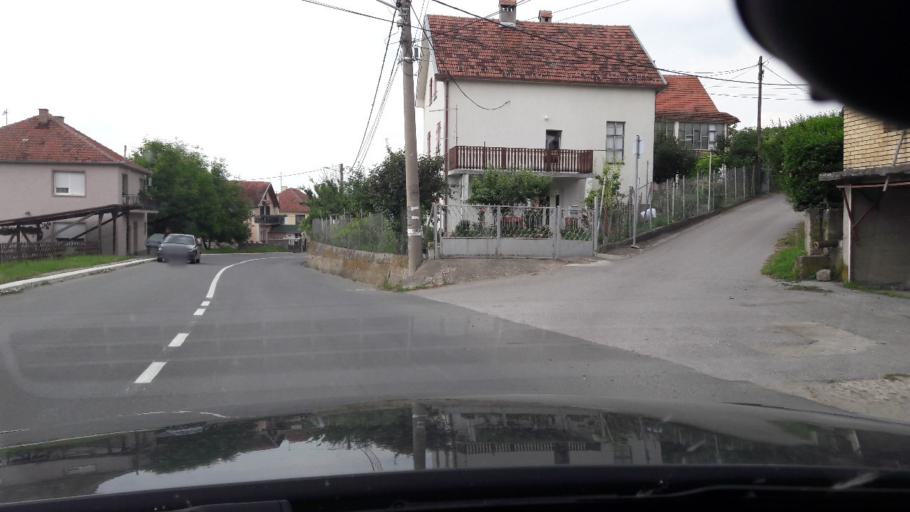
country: RS
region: Central Serbia
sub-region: Belgrade
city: Grocka
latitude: 44.6643
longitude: 20.5944
